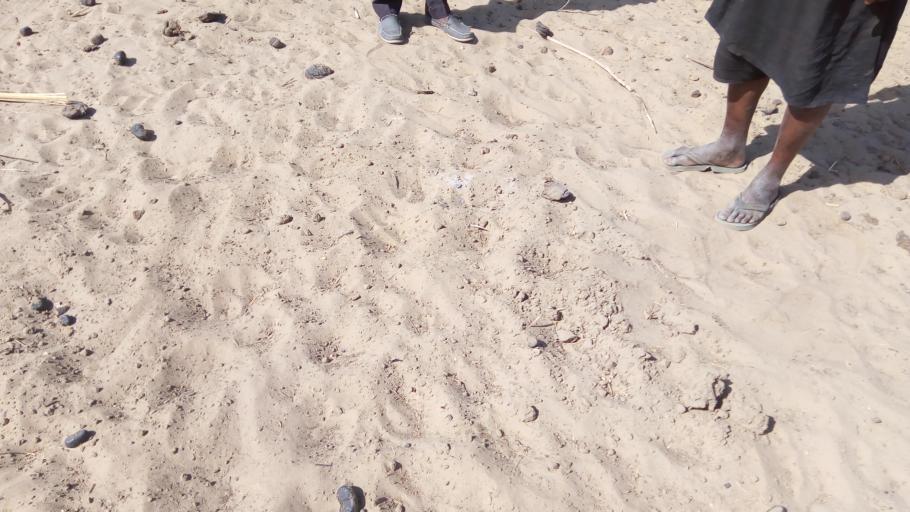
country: ML
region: Kayes
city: Diema
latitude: 14.5131
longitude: -8.8394
